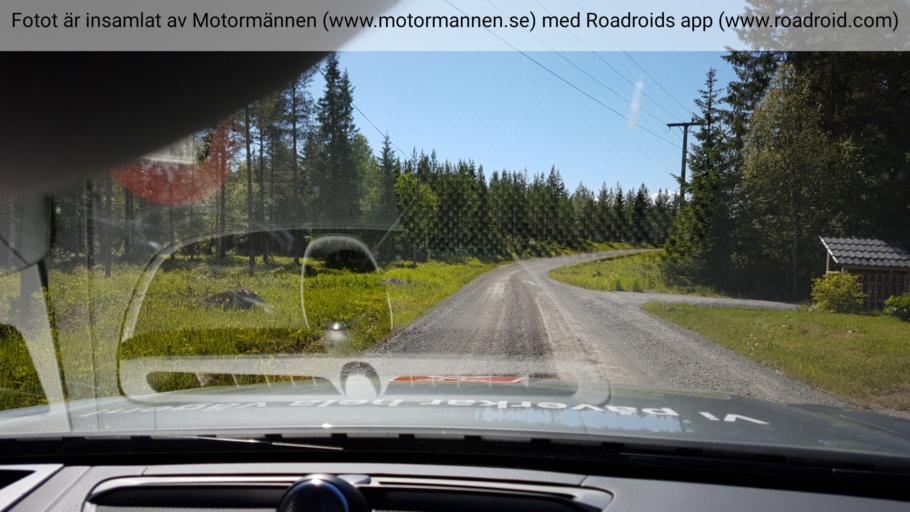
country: SE
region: Jaemtland
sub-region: OEstersunds Kommun
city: Brunflo
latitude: 62.9712
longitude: 14.6862
